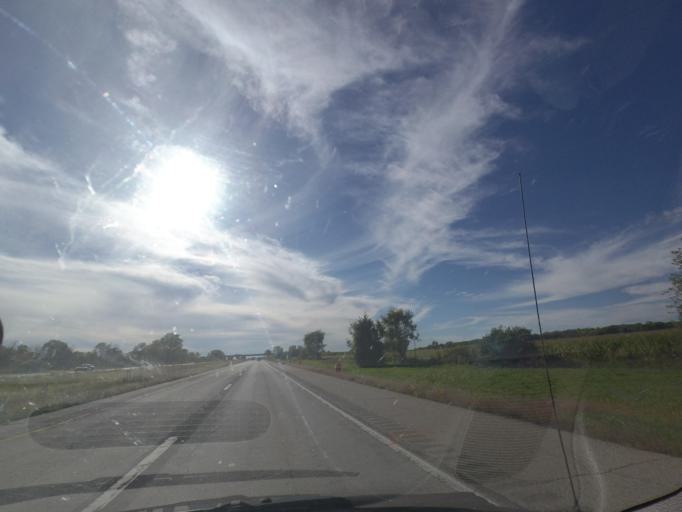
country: US
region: Illinois
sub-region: Macon County
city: Harristown
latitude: 39.8342
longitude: -89.0701
